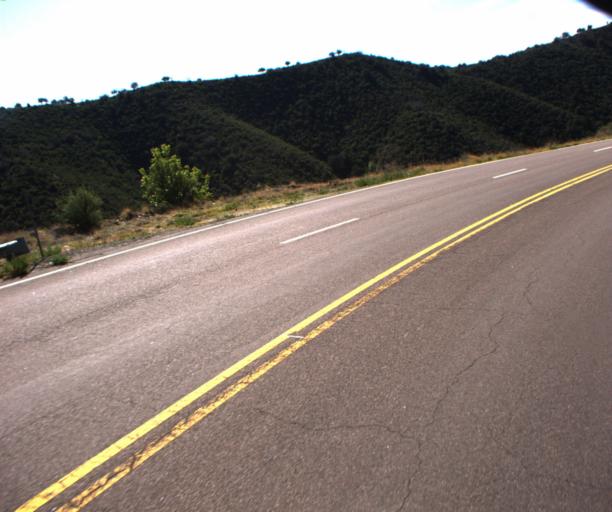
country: US
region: Arizona
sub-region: Yavapai County
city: Prescott
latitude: 34.4702
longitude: -112.5154
